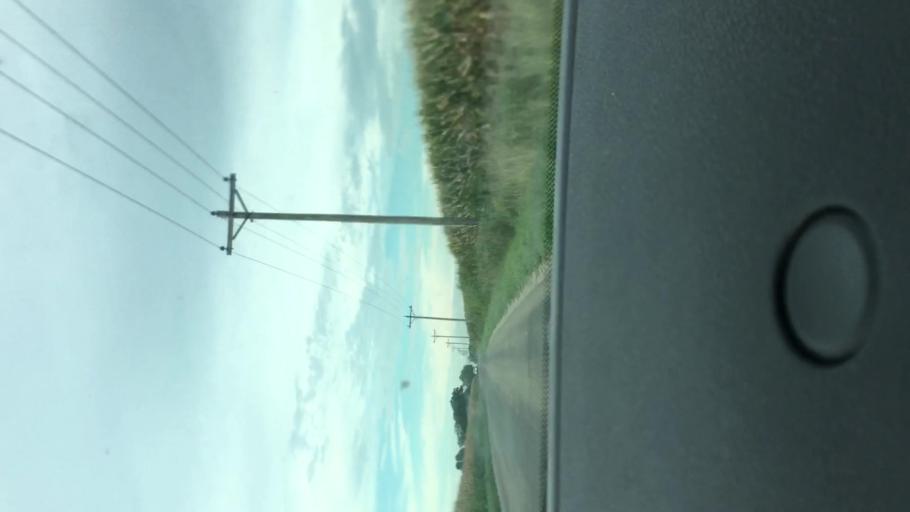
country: US
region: Indiana
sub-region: Jay County
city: Portland
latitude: 40.4354
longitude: -84.9207
